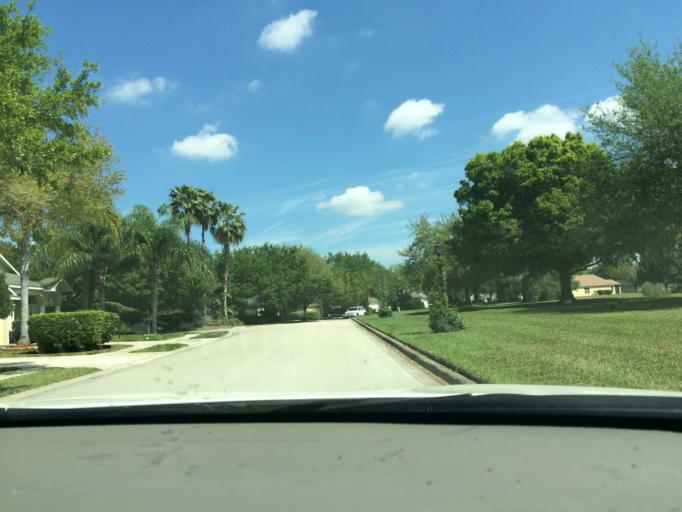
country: US
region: Florida
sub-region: Sarasota County
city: The Meadows
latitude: 27.4278
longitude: -82.4162
